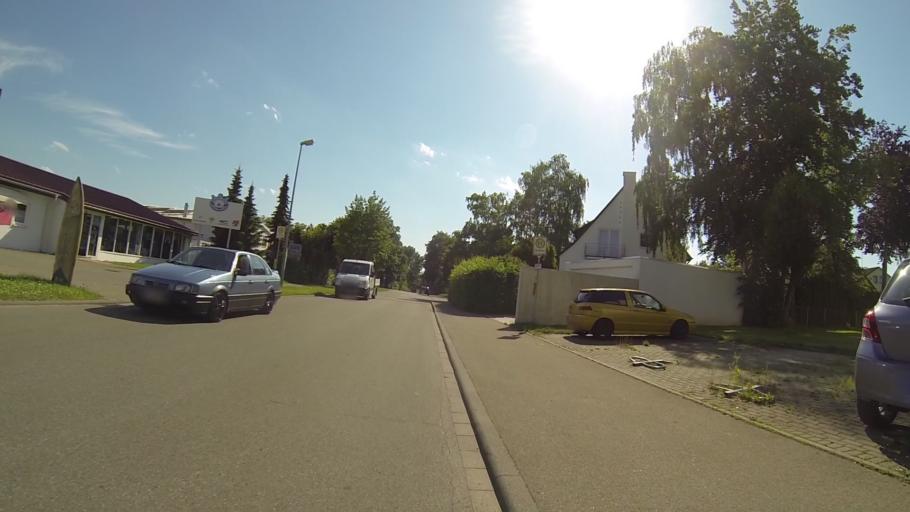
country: DE
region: Baden-Wuerttemberg
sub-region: Tuebingen Region
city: Laupheim
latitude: 48.2216
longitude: 9.8729
